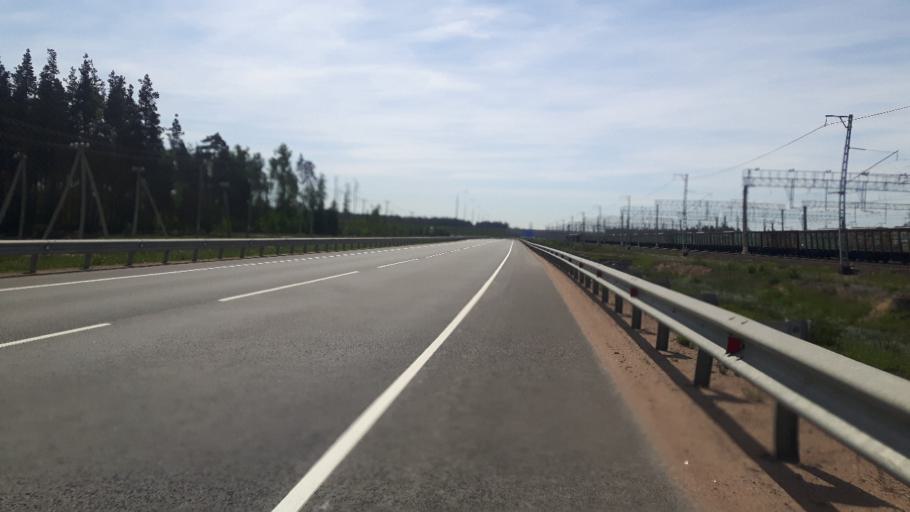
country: RU
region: Leningrad
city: Vistino
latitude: 59.6690
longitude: 28.4333
